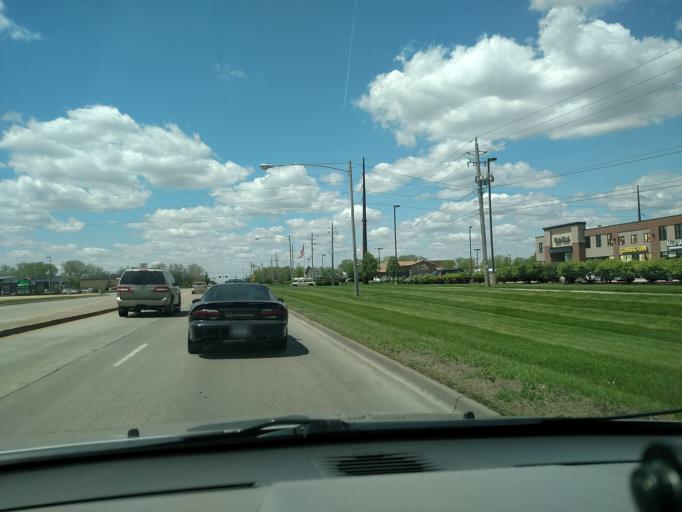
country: US
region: Iowa
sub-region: Polk County
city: Ankeny
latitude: 41.7029
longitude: -93.5848
